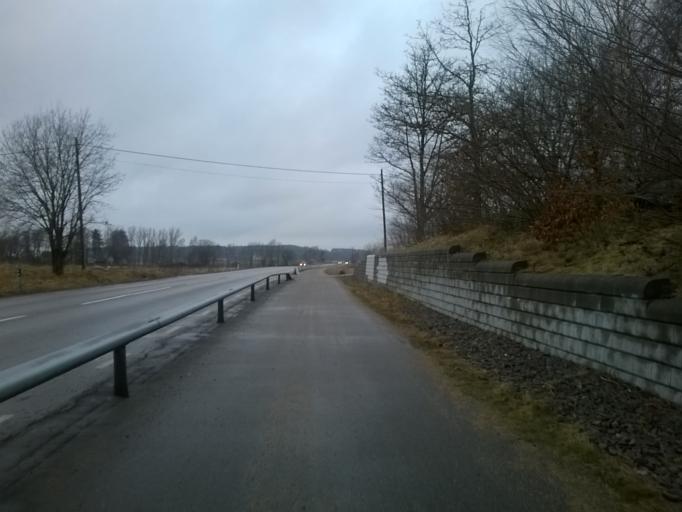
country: SE
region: Vaestra Goetaland
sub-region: Kungalvs Kommun
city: Kungalv
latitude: 57.8995
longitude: 11.9315
